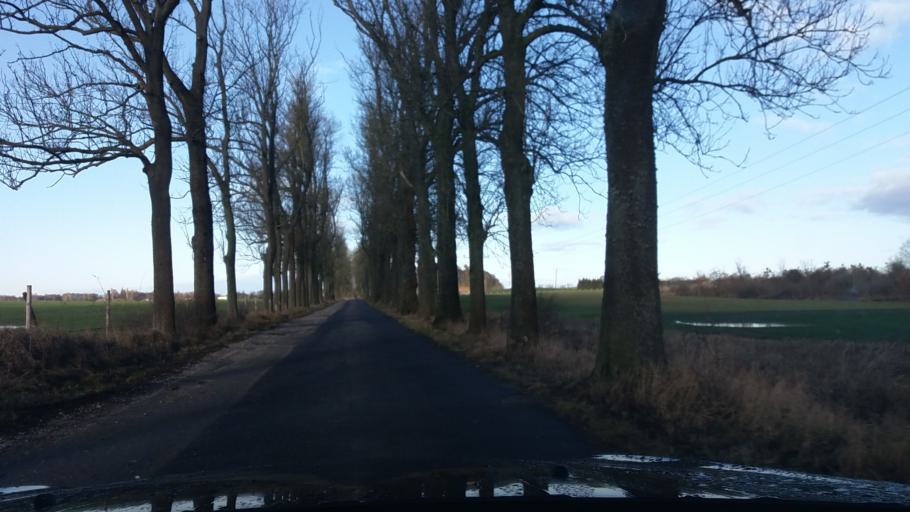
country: PL
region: West Pomeranian Voivodeship
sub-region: Powiat choszczenski
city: Drawno
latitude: 53.2047
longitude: 15.7777
